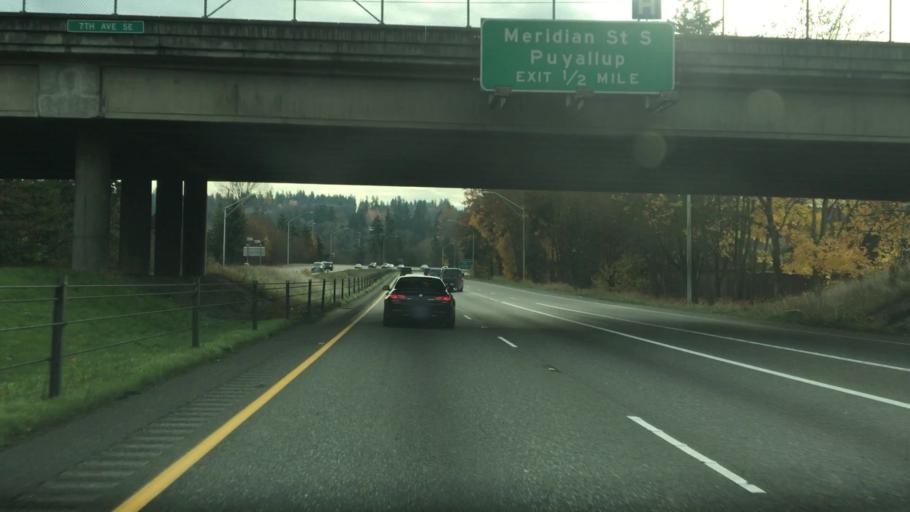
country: US
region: Washington
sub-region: Pierce County
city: Puyallup
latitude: 47.1864
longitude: -122.2831
